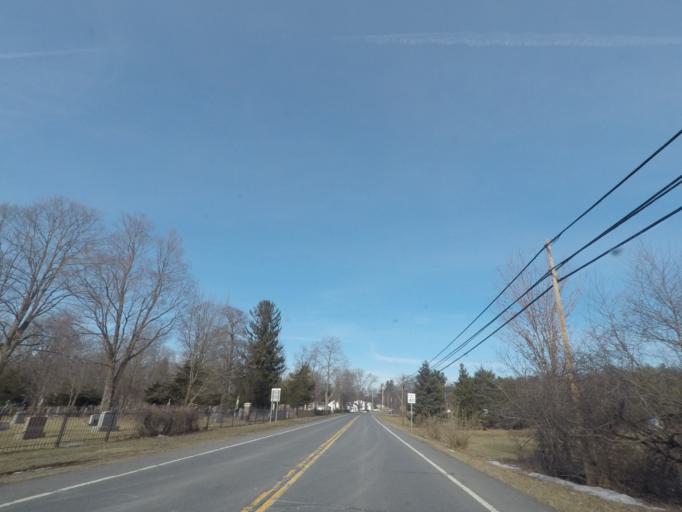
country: US
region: New York
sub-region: Rensselaer County
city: Nassau
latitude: 42.5025
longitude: -73.6167
